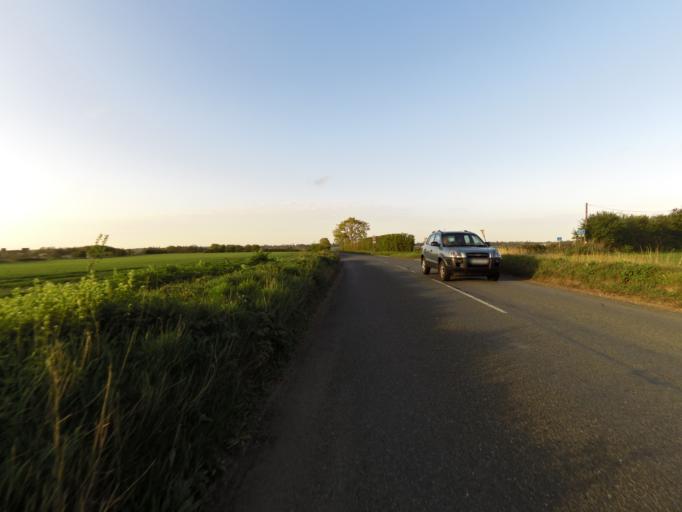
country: GB
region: England
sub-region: Suffolk
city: Bramford
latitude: 52.0461
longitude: 1.0940
